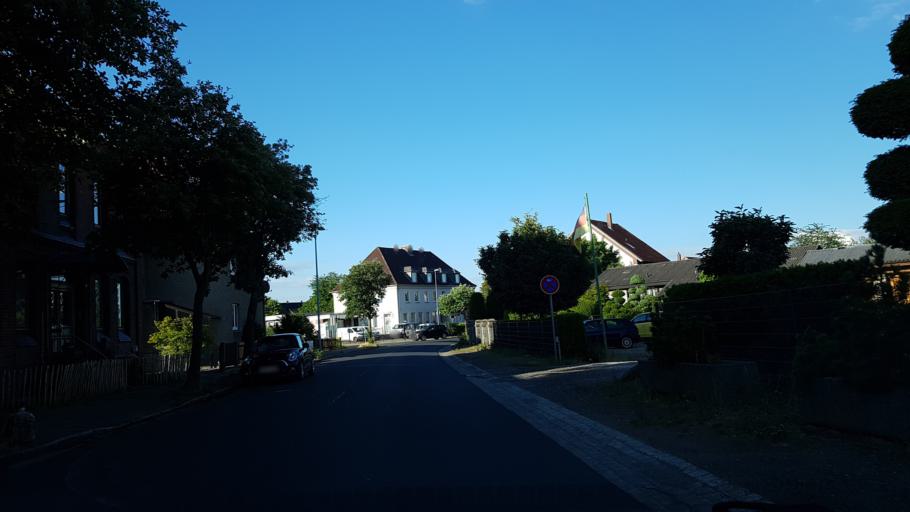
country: DE
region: Lower Saxony
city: Nordstemmen
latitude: 52.1948
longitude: 9.7768
